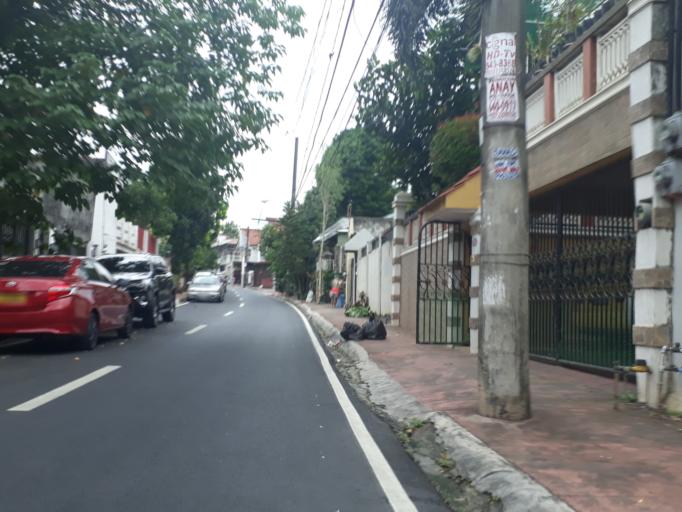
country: PH
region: Calabarzon
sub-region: Province of Rizal
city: Antipolo
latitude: 14.6435
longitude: 121.1190
